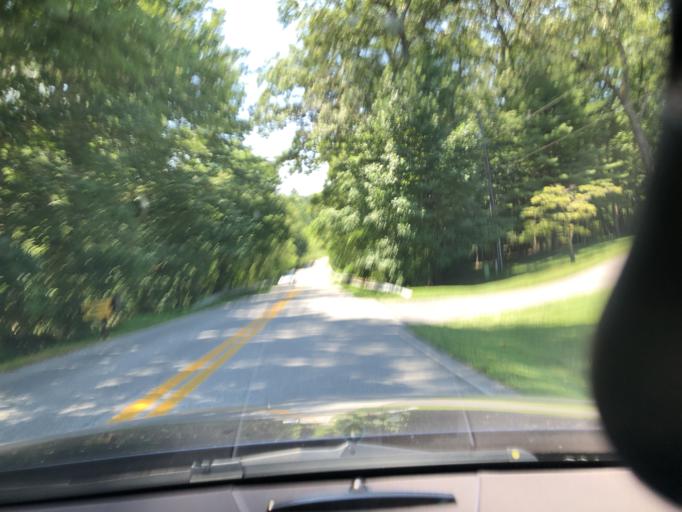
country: US
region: Maryland
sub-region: Carroll County
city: Westminster
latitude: 39.5113
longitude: -76.9253
